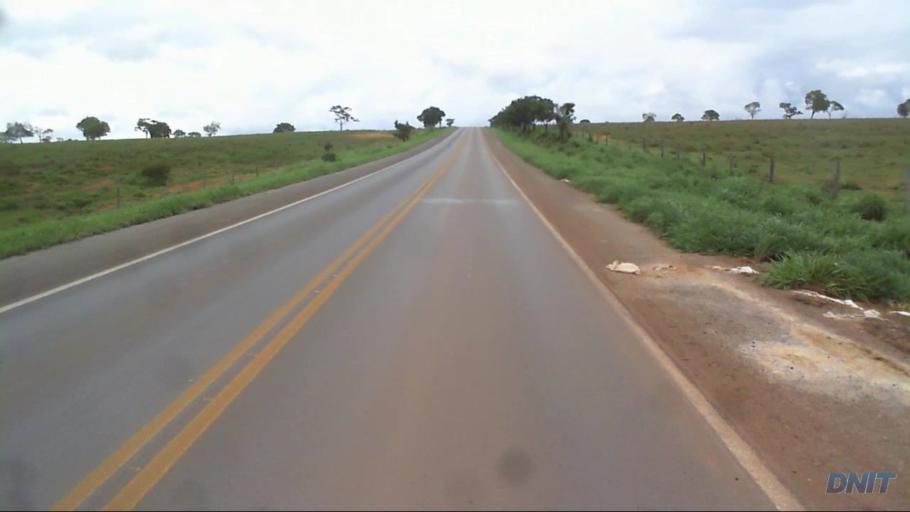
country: BR
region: Goias
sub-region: Padre Bernardo
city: Padre Bernardo
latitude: -15.1577
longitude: -48.3189
